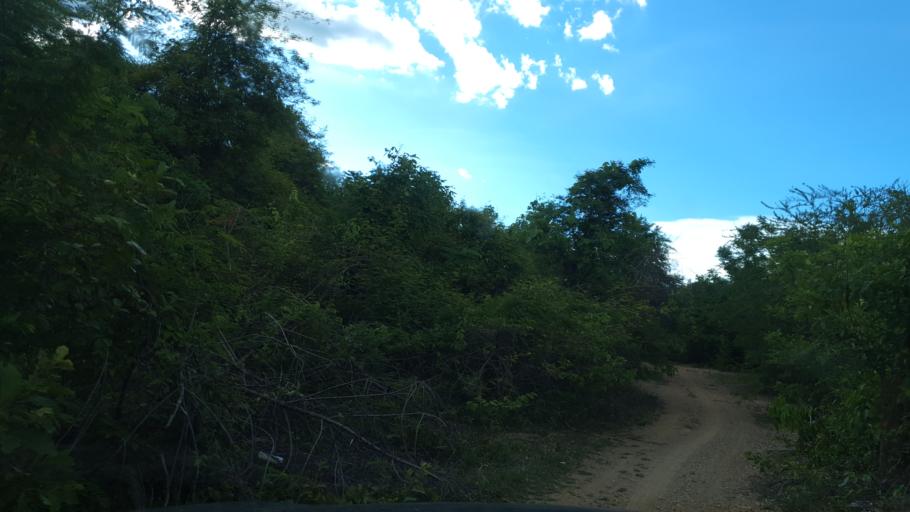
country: TH
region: Lampang
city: Sop Prap
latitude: 17.8864
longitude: 99.2894
